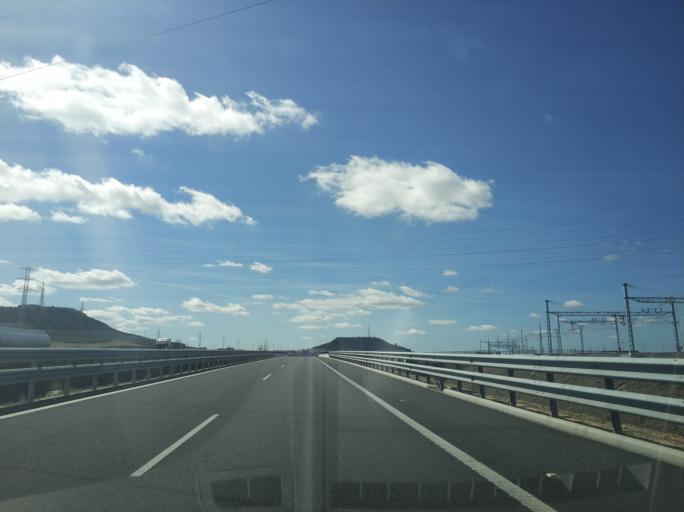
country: ES
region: Castille and Leon
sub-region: Provincia de Valladolid
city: Cisterniga
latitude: 41.6418
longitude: -4.6752
